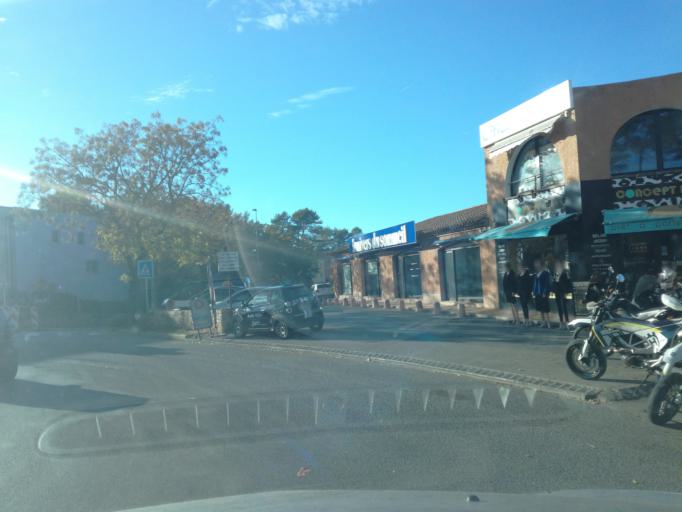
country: FR
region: Provence-Alpes-Cote d'Azur
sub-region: Departement des Alpes-Maritimes
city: Mouans-Sartoux
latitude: 43.6135
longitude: 6.9694
